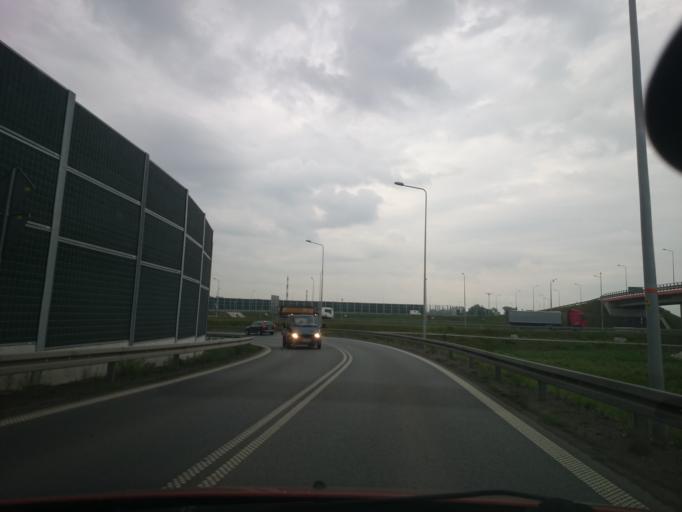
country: PL
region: Opole Voivodeship
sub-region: Powiat opolski
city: Czarnowasy
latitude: 50.7036
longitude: 17.9031
